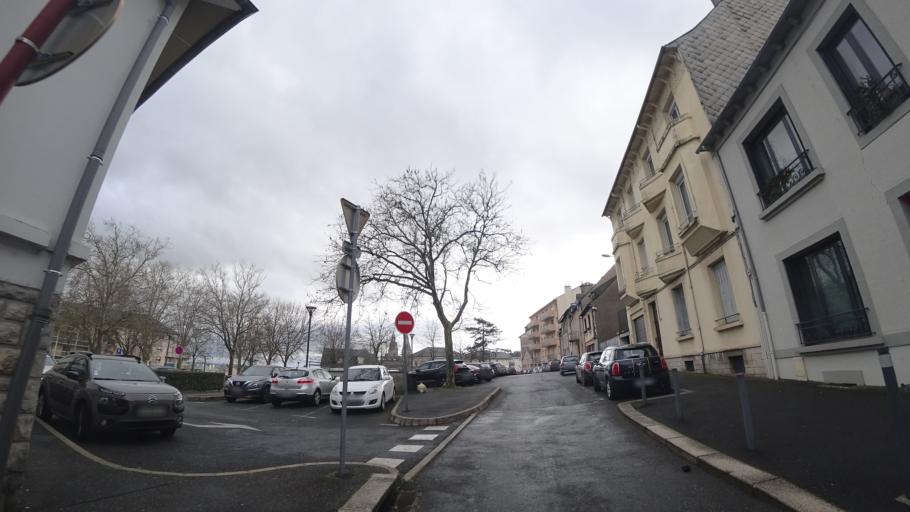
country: FR
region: Midi-Pyrenees
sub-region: Departement de l'Aveyron
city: Rodez
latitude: 44.3561
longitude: 2.5733
